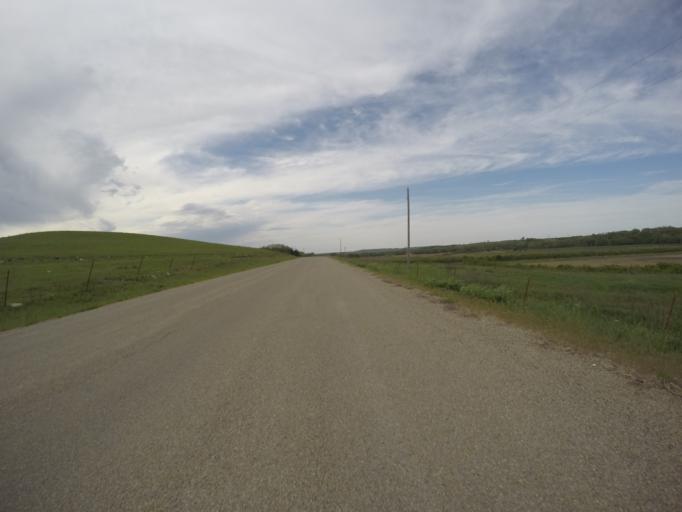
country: US
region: Kansas
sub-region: Riley County
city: Ogden
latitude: 39.0138
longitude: -96.6052
